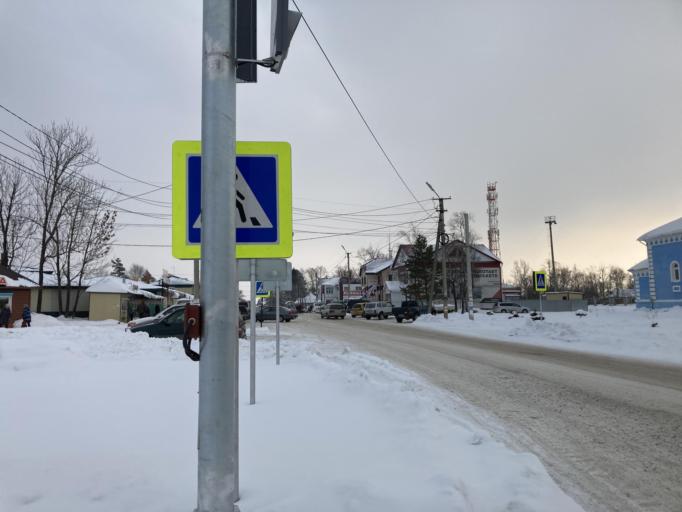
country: RU
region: Khabarovsk Krai
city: Khor
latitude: 47.9655
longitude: 135.0535
